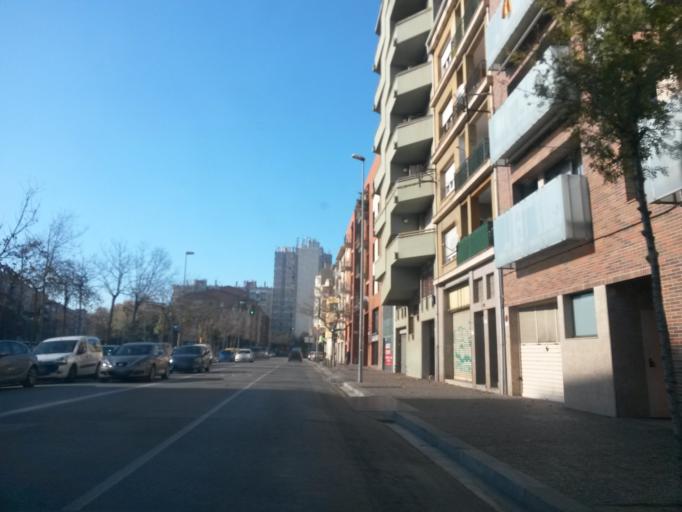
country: ES
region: Catalonia
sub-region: Provincia de Girona
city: Girona
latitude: 41.9848
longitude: 2.8161
